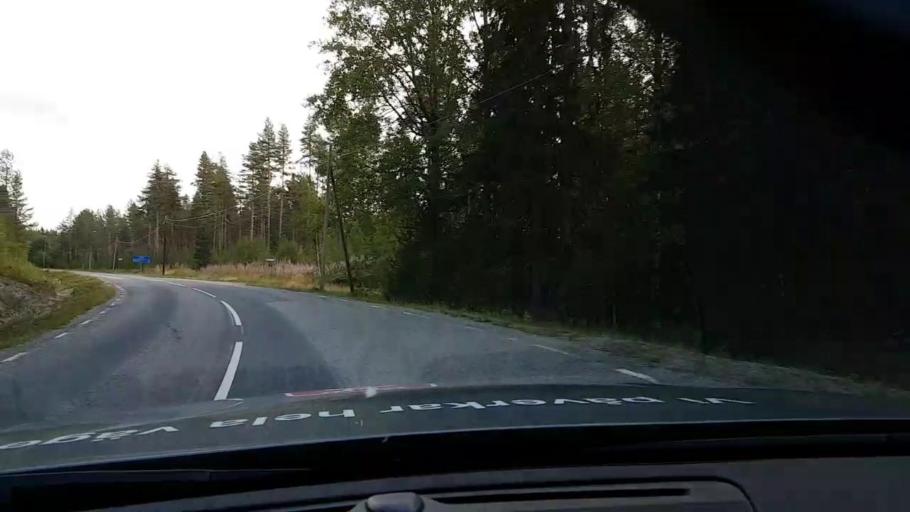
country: SE
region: Vaesterbotten
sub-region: Asele Kommun
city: Asele
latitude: 63.7948
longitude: 17.5677
